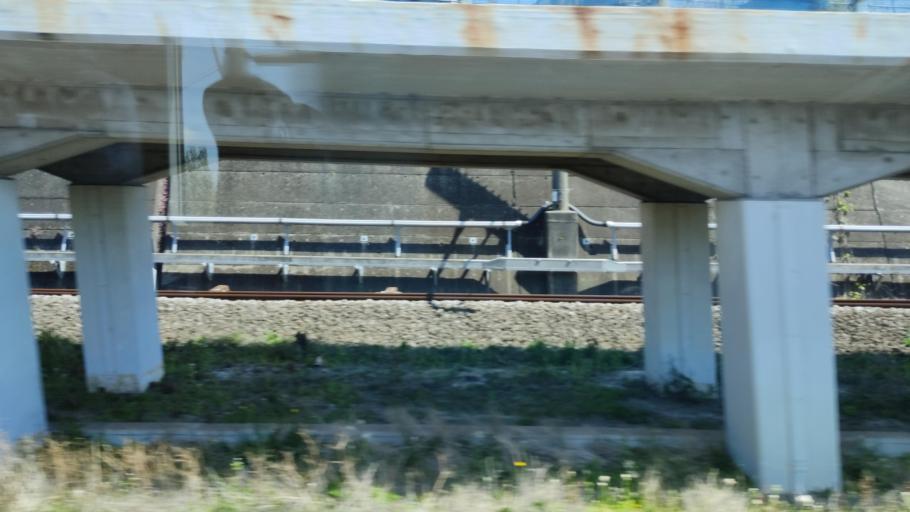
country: JP
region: Kanagawa
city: Kamakura
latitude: 35.3698
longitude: 139.5296
